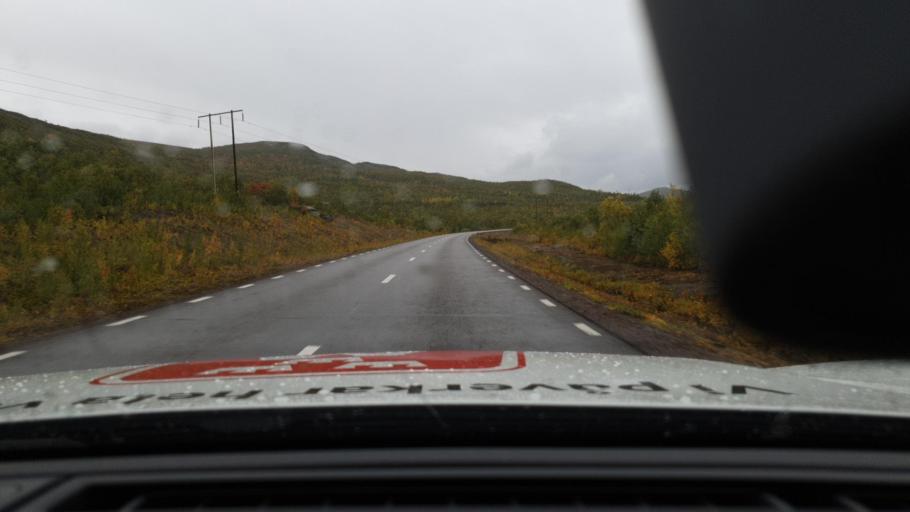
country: SE
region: Norrbotten
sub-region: Kiruna Kommun
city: Kiruna
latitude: 68.2388
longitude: 19.5304
